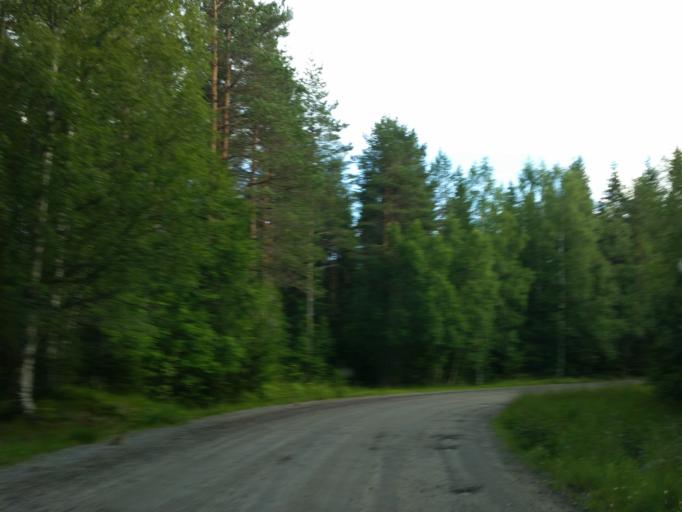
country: SE
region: Vaesterbotten
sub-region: Robertsfors Kommun
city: Robertsfors
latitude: 64.0451
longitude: 20.8508
